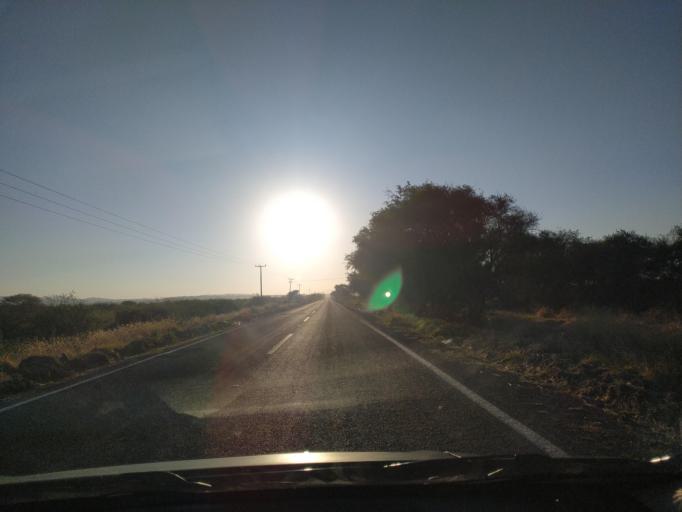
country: MX
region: Guanajuato
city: Ciudad Manuel Doblado
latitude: 20.7378
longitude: -101.8651
